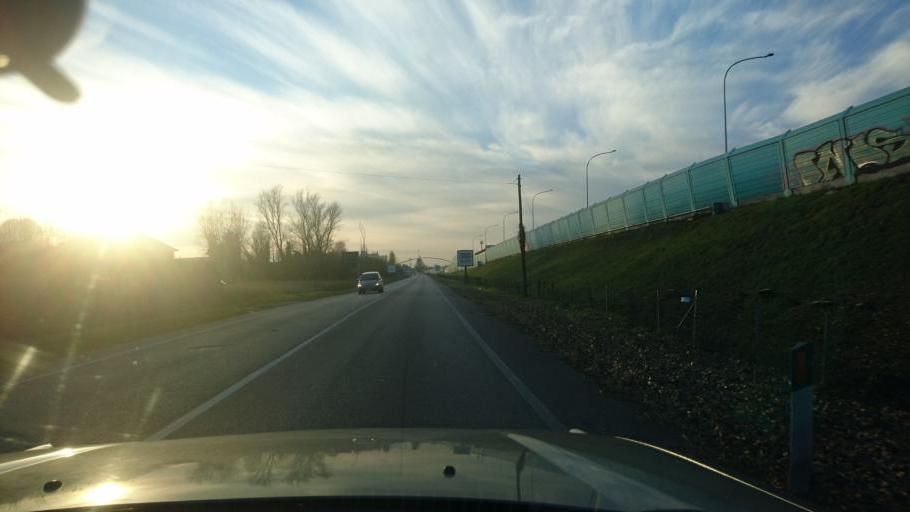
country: IT
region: Veneto
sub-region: Provincia di Padova
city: Noventa
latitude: 45.4192
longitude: 11.9457
